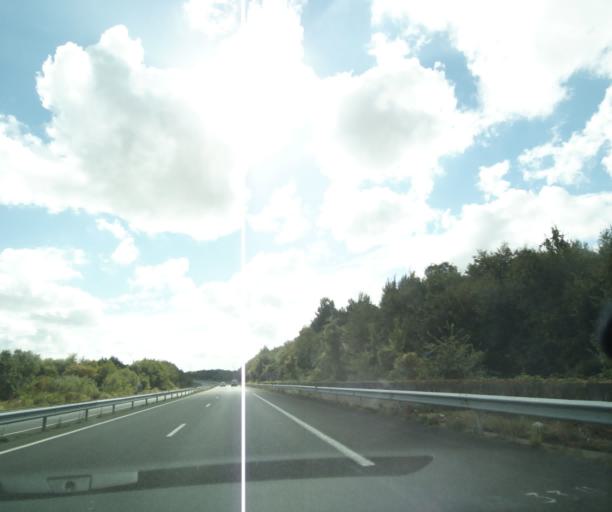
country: FR
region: Poitou-Charentes
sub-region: Departement de la Charente-Maritime
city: Saint-Georges-des-Coteaux
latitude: 45.8093
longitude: -0.6962
